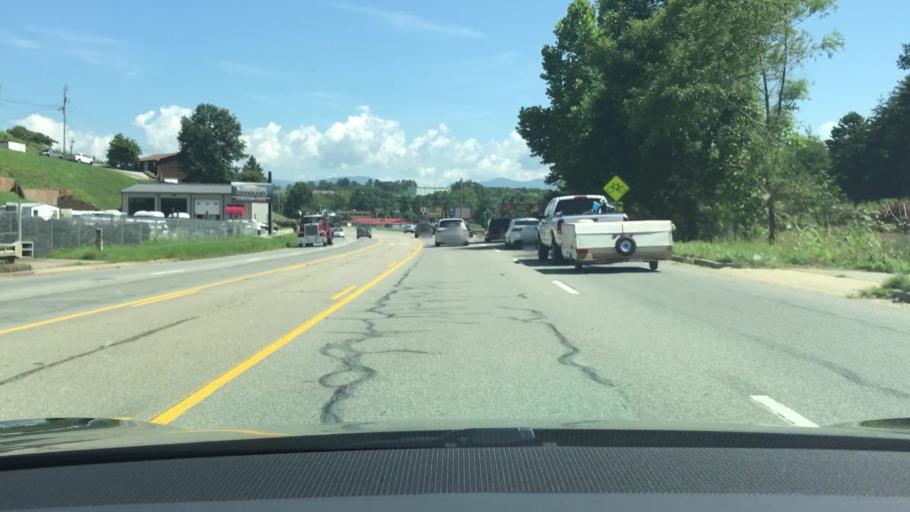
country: US
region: North Carolina
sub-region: Macon County
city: Franklin
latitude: 35.1522
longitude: -83.3924
